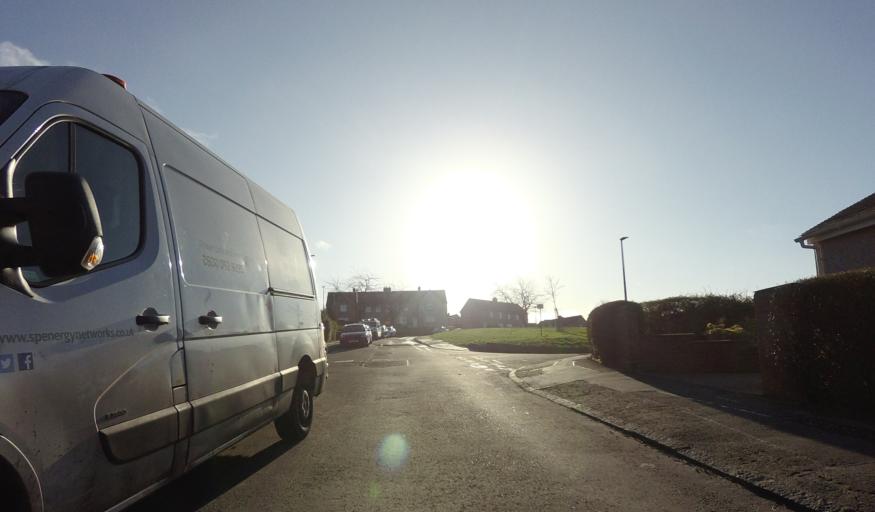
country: GB
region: Scotland
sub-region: Edinburgh
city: Colinton
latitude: 55.9602
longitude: -3.2825
